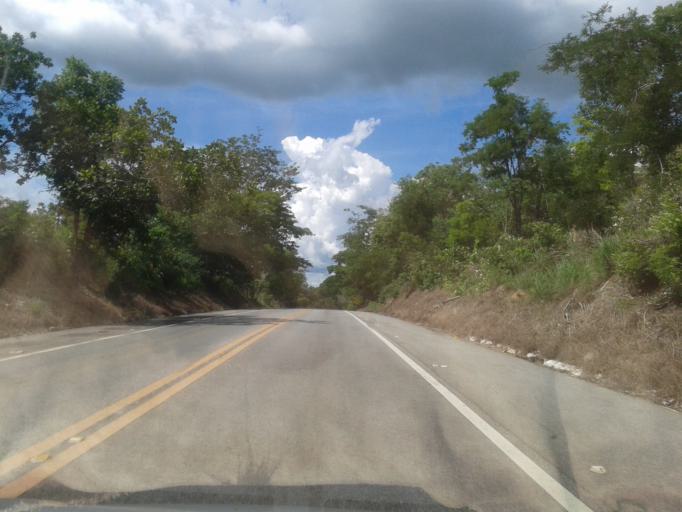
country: BR
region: Goias
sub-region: Goias
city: Goias
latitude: -15.8121
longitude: -50.1196
